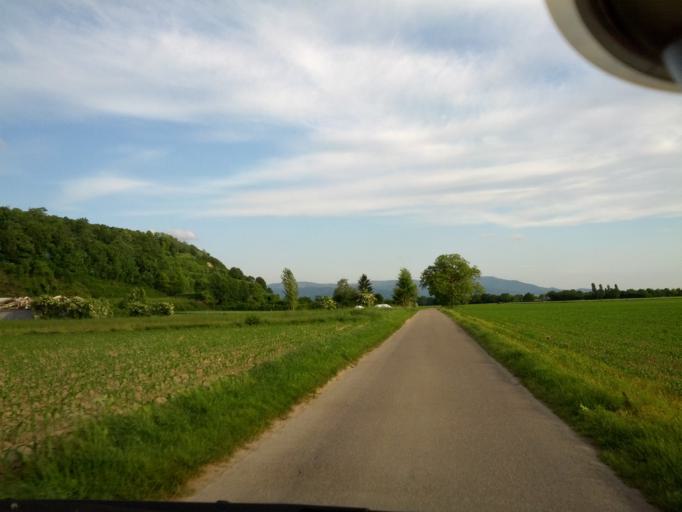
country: DE
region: Baden-Wuerttemberg
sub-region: Freiburg Region
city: Merdingen
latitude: 47.9775
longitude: 7.6730
